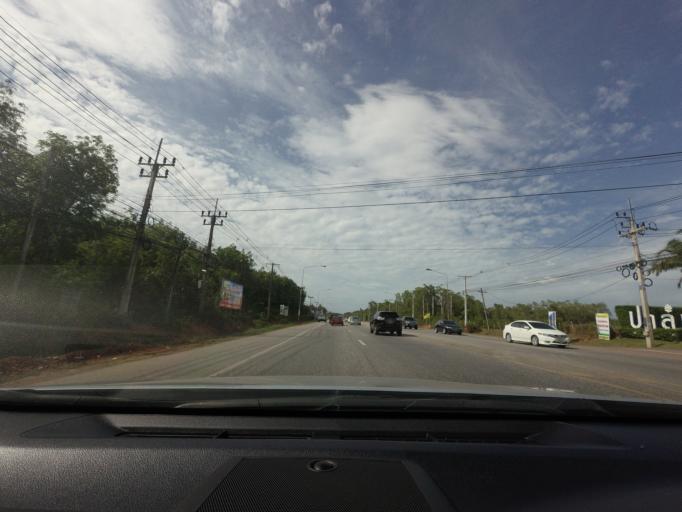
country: TH
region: Songkhla
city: Khlong Hoi Khong
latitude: 6.9604
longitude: 100.4237
